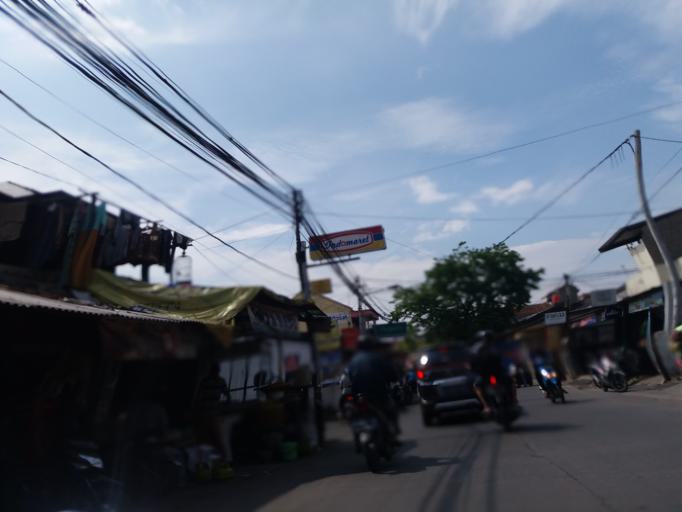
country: ID
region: West Java
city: Bandung
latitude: -6.9221
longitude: 107.6453
